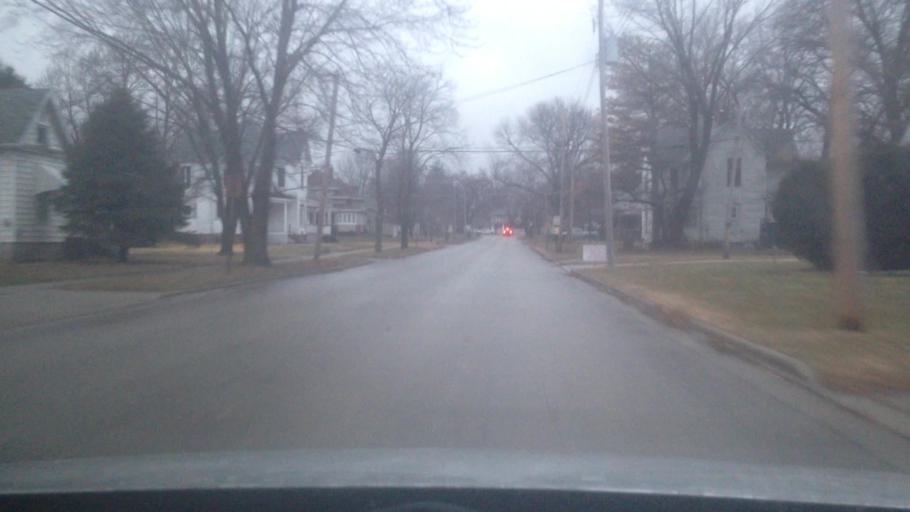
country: US
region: Illinois
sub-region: Christian County
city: Pana
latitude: 39.3832
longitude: -89.0786
